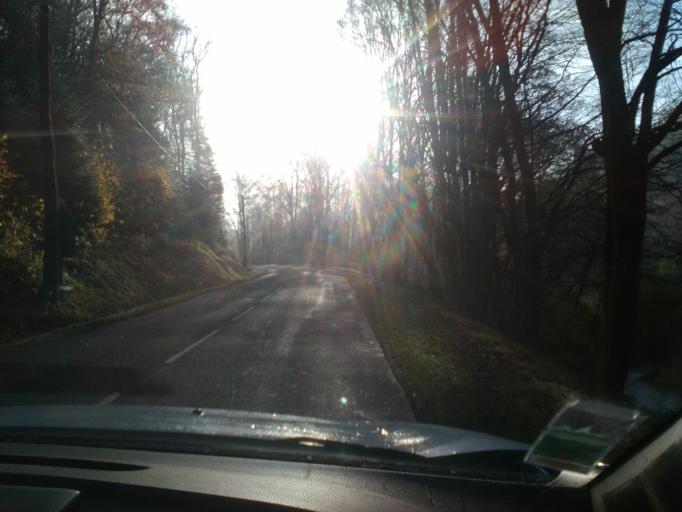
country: FR
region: Lorraine
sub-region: Departement des Vosges
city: Uzemain
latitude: 48.0689
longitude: 6.3157
